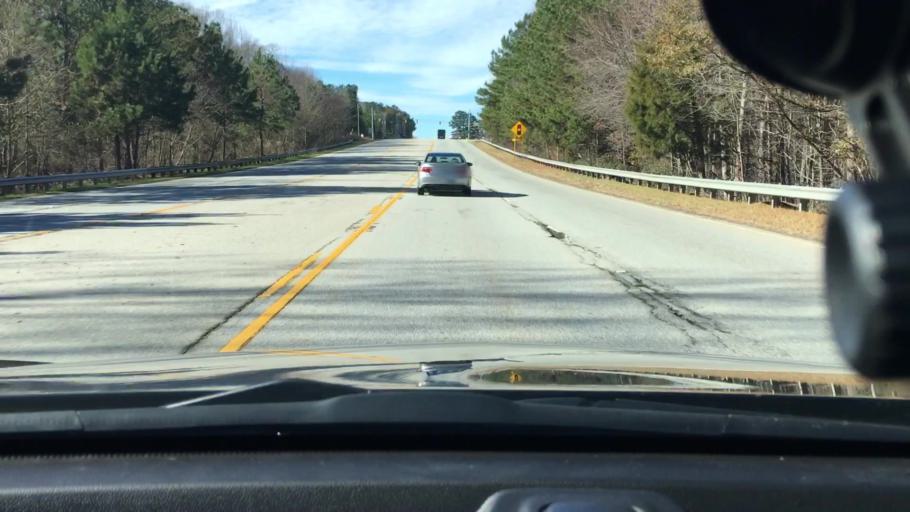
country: US
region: South Carolina
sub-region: Spartanburg County
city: Pacolet
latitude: 34.9252
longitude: -81.8340
